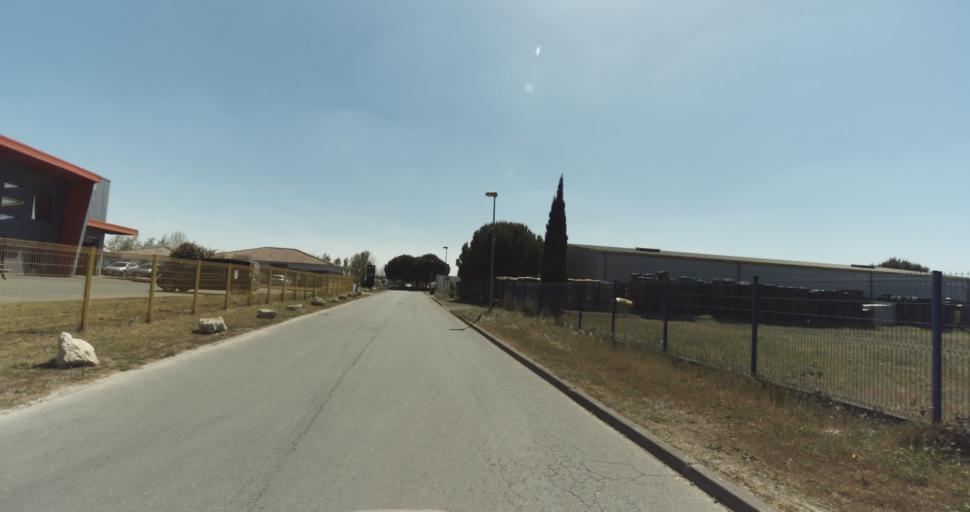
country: FR
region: Aquitaine
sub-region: Departement de la Gironde
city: Martignas-sur-Jalle
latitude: 44.8088
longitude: -0.7487
